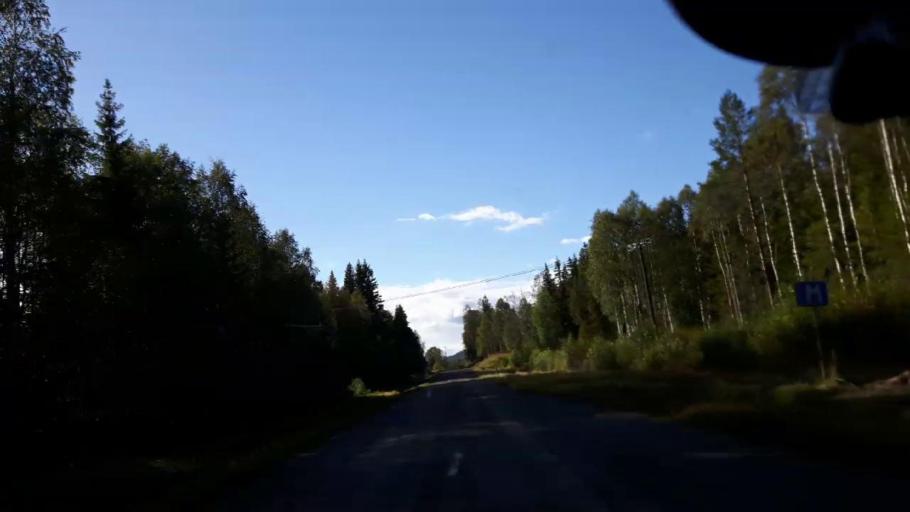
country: SE
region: Jaemtland
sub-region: Ragunda Kommun
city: Hammarstrand
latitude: 63.4910
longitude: 16.0505
